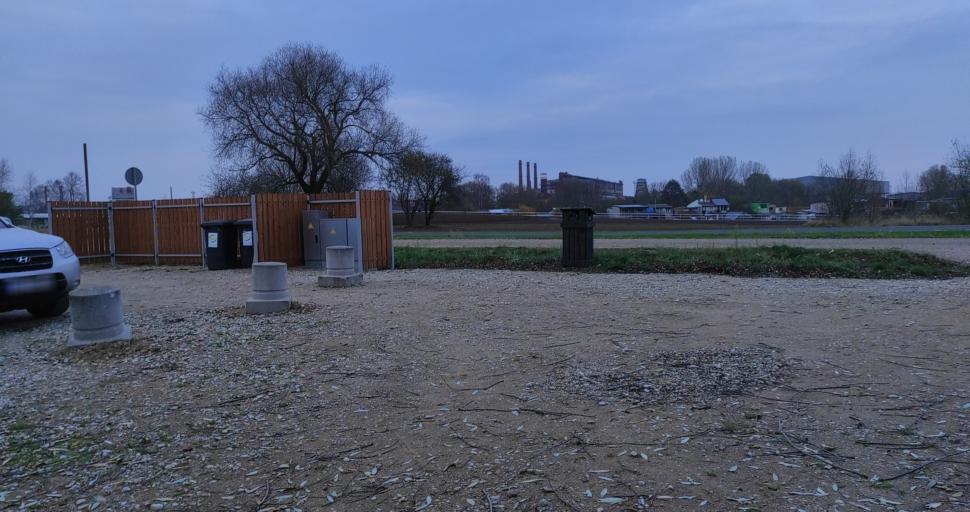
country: LV
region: Liepaja
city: Liepaja
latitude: 56.5164
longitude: 21.0328
